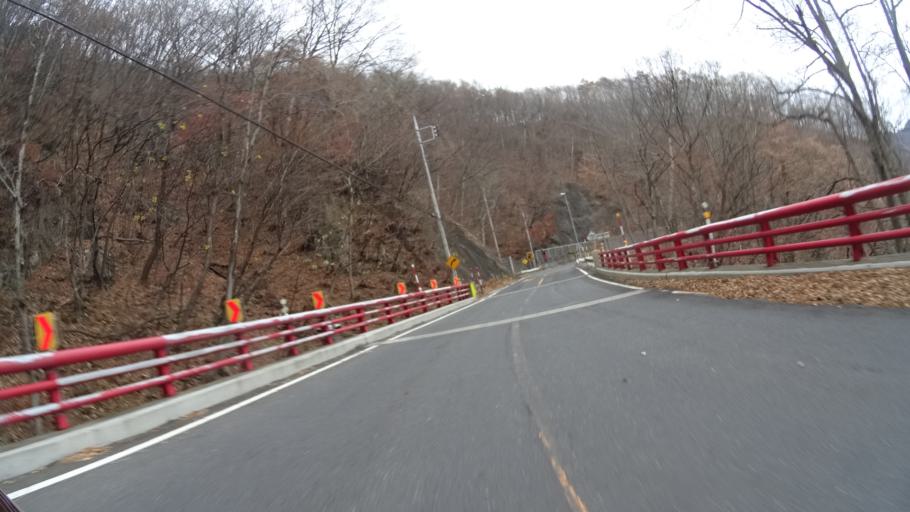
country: JP
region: Gunma
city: Nakanojomachi
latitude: 36.7322
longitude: 138.8385
